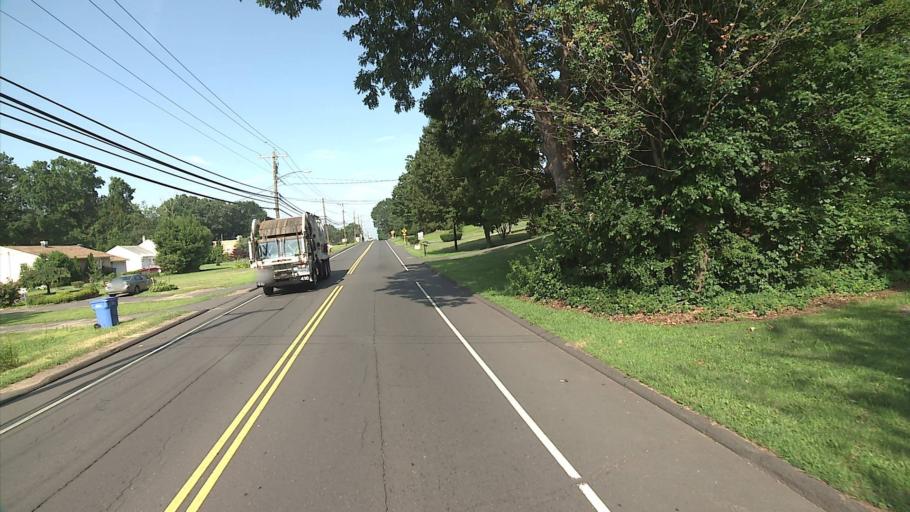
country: US
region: Connecticut
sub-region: New Haven County
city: Wolcott
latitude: 41.5529
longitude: -72.9799
